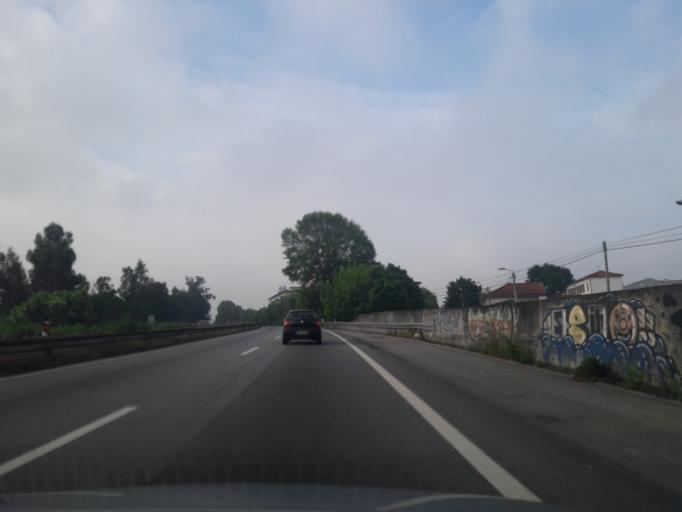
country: PT
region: Porto
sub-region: Matosinhos
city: Senhora da Hora
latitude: 41.1948
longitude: -8.6285
